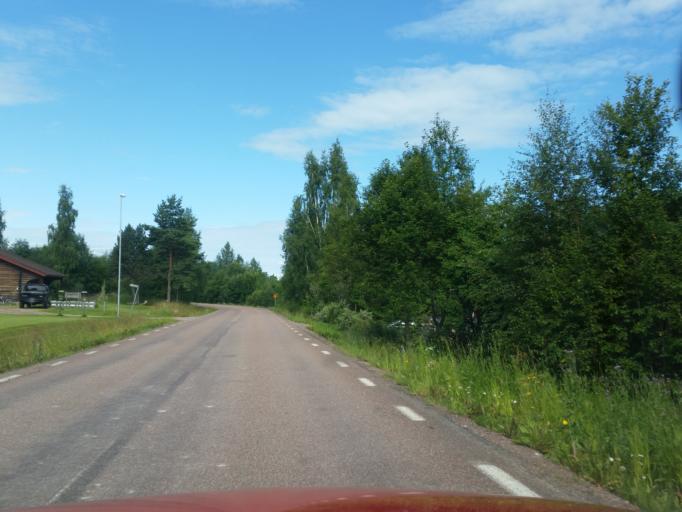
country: SE
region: Dalarna
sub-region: Leksand Municipality
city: Smedby
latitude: 60.6769
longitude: 15.1284
